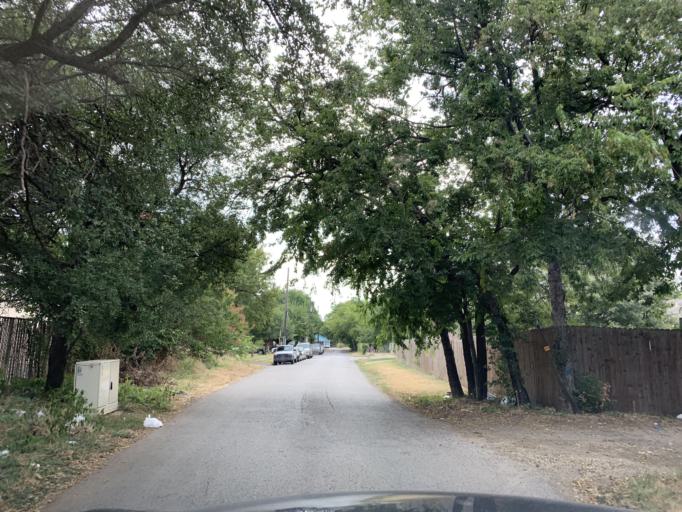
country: US
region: Texas
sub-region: Dallas County
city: Cockrell Hill
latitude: 32.7535
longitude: -96.8721
